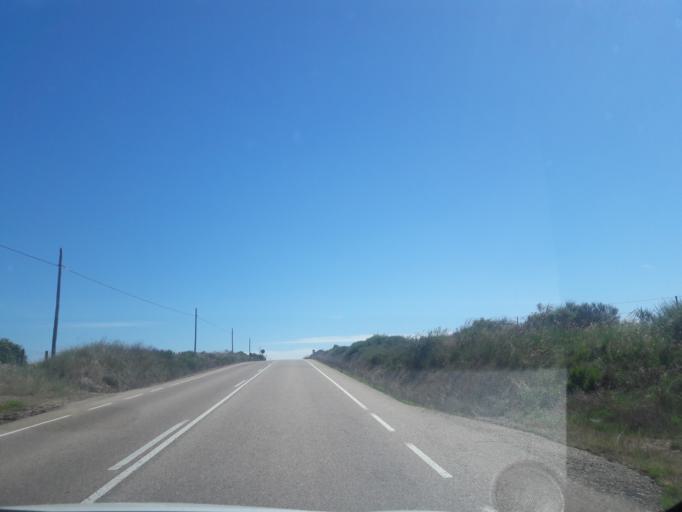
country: ES
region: Castille and Leon
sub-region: Provincia de Salamanca
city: Guadramiro
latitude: 41.0063
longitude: -6.5015
